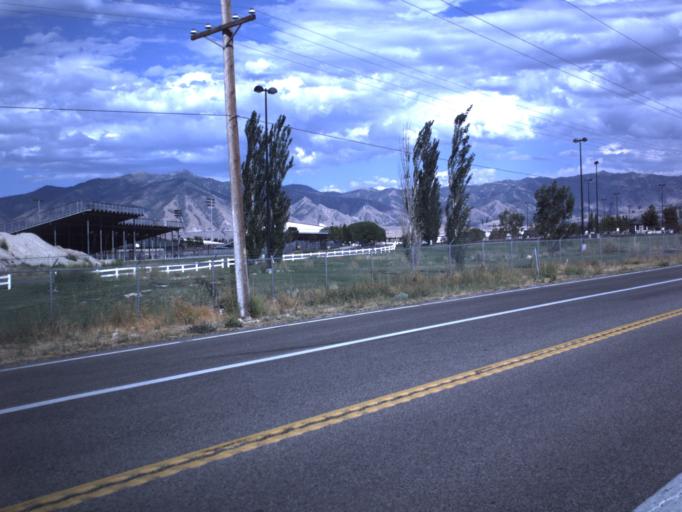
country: US
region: Utah
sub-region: Tooele County
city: Erda
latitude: 40.5715
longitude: -112.3778
